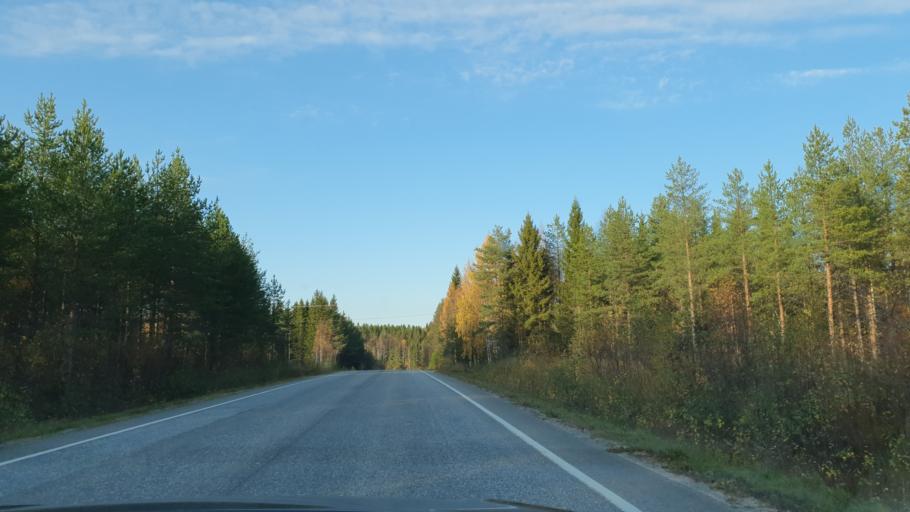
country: FI
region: Kainuu
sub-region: Kehys-Kainuu
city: Kuhmo
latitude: 64.1564
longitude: 29.4639
